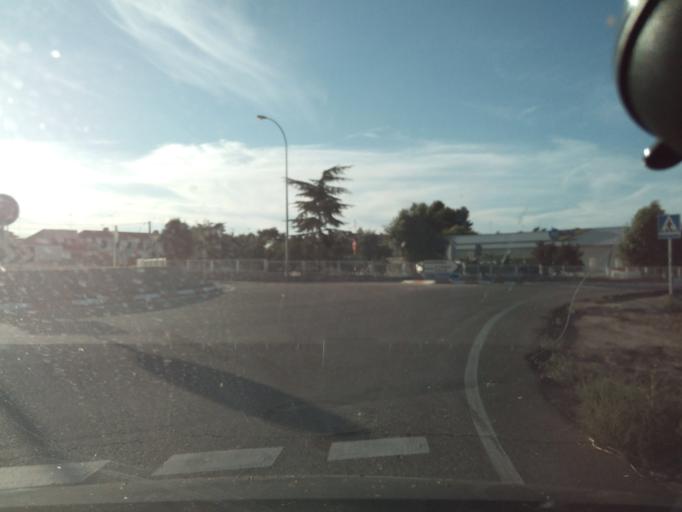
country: ES
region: Castille-La Mancha
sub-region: Province of Toledo
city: Tembleque
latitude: 39.6895
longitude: -3.5019
